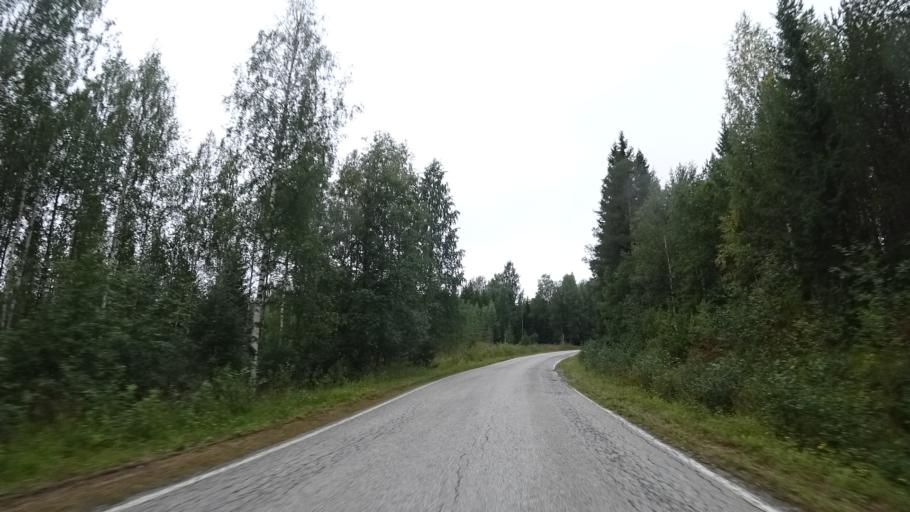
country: FI
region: North Karelia
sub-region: Pielisen Karjala
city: Lieksa
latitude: 63.3229
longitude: 30.2307
